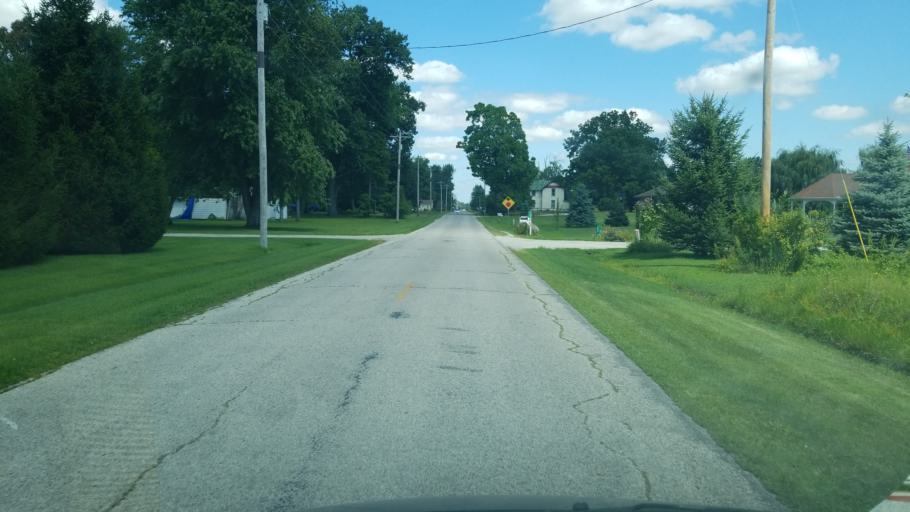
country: US
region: Ohio
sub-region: Henry County
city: Liberty Center
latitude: 41.4985
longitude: -83.9413
